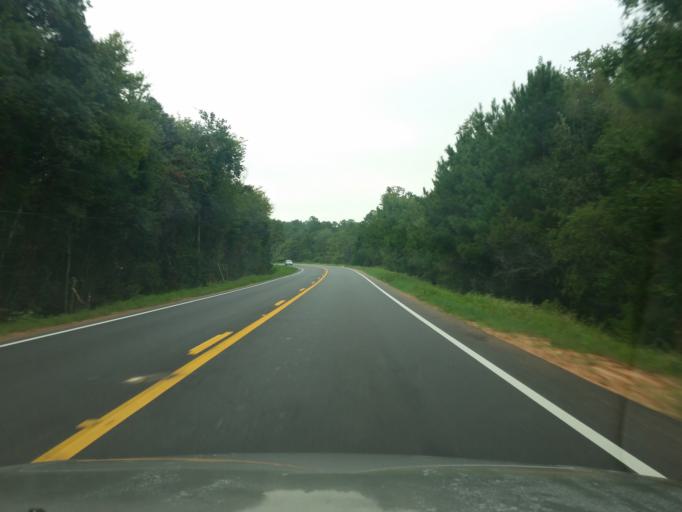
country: US
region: Alabama
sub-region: Baldwin County
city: Spanish Fort
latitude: 30.7040
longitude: -87.9019
